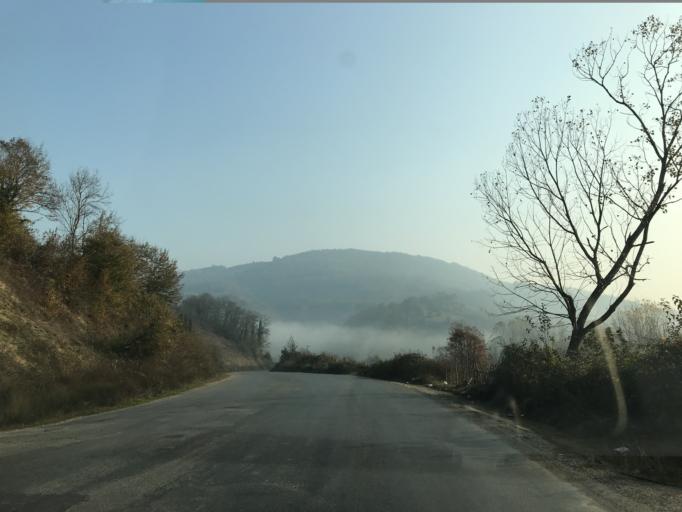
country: TR
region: Duzce
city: Cumayeri
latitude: 40.8906
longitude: 30.9539
